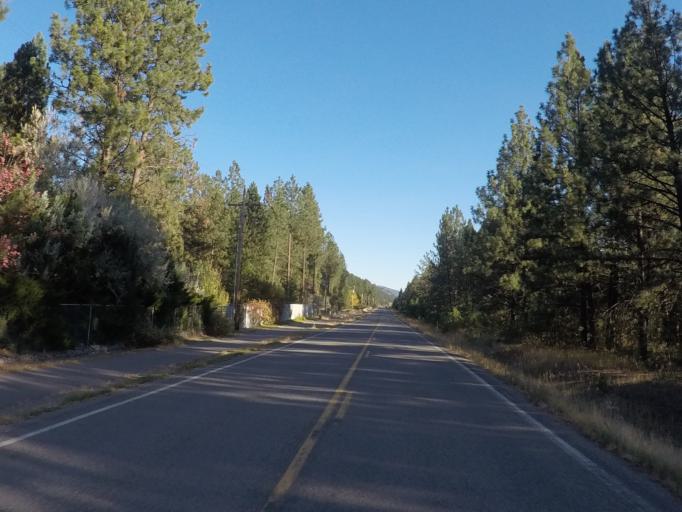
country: US
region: Montana
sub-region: Missoula County
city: Bonner-West Riverside
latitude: 46.8427
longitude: -113.8385
